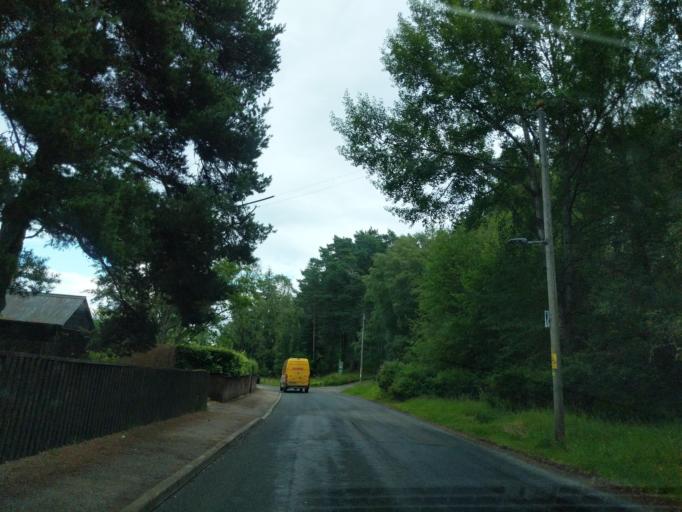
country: GB
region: Scotland
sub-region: Highland
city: Aviemore
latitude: 57.2831
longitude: -3.8207
